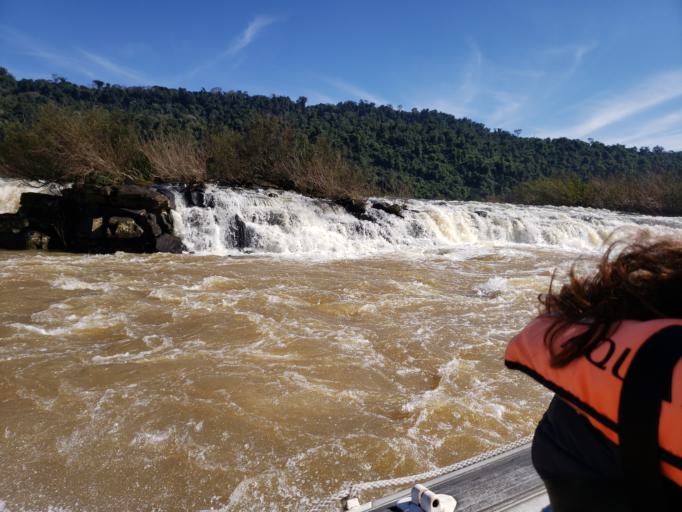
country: BR
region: Rio Grande do Sul
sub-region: Tres Passos
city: Tres Passos
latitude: -27.1464
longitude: -53.8867
